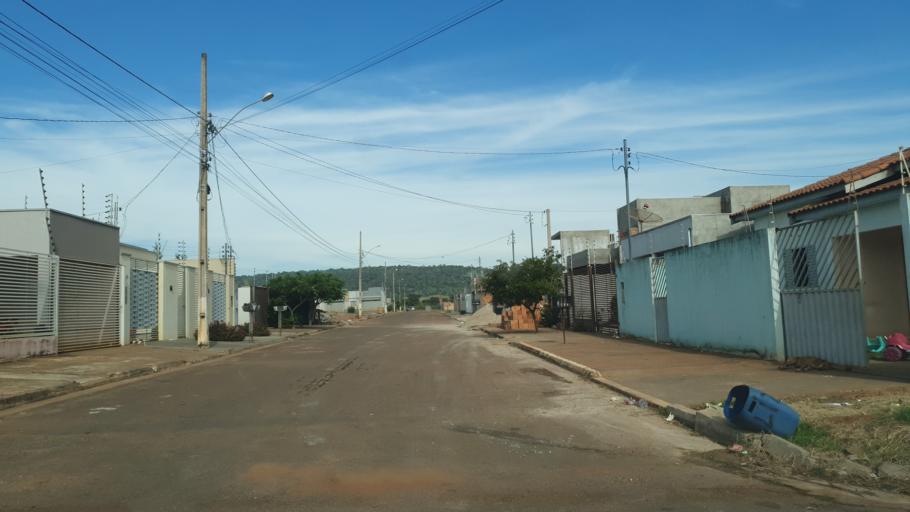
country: BR
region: Mato Grosso
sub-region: Pontes E Lacerda
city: Pontes e Lacerda
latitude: -15.2492
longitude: -59.3181
